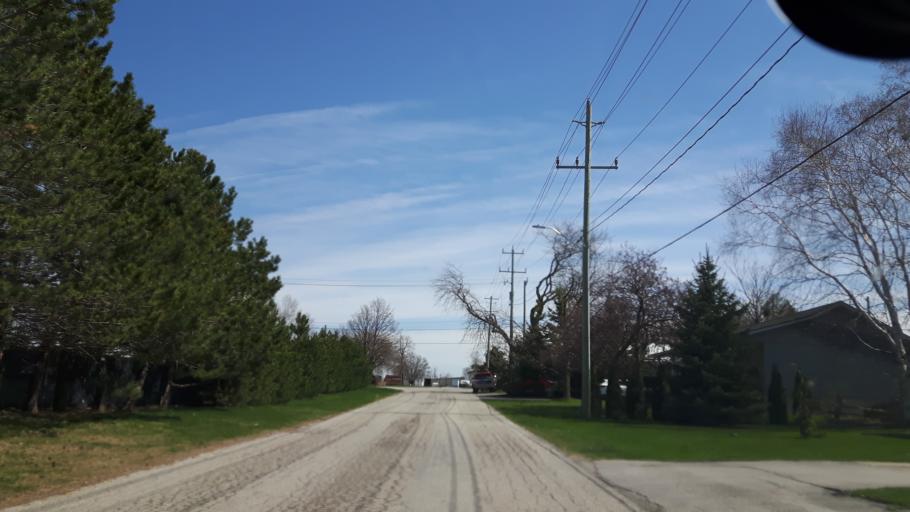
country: CA
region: Ontario
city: Goderich
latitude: 43.7367
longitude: -81.6955
